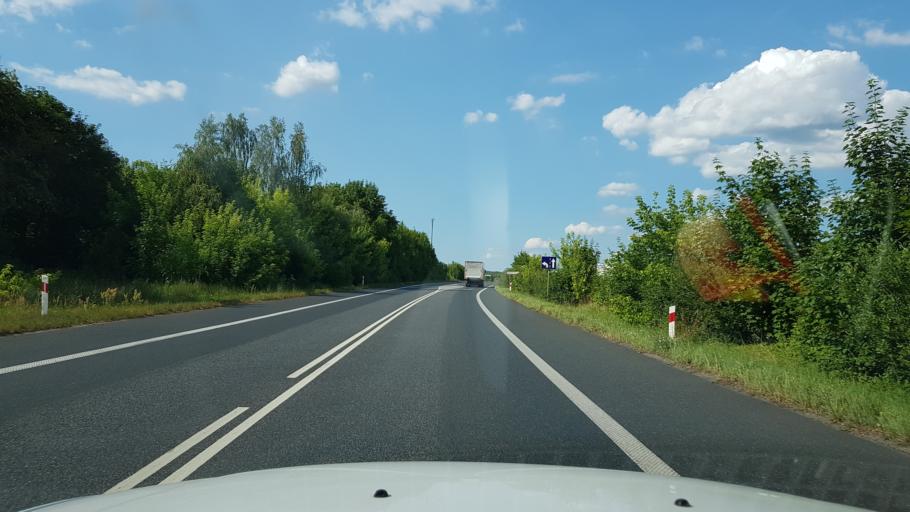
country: PL
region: West Pomeranian Voivodeship
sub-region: Powiat gryfinski
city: Stare Czarnowo
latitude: 53.2728
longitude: 14.7812
